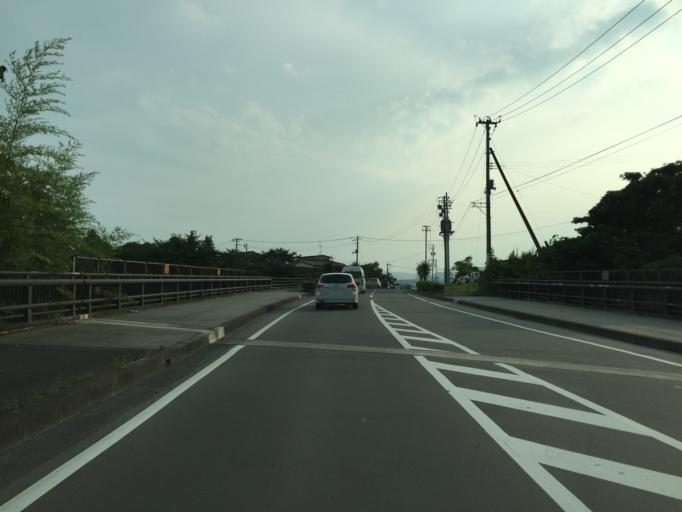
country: JP
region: Miyagi
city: Marumori
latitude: 37.8099
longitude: 140.9237
